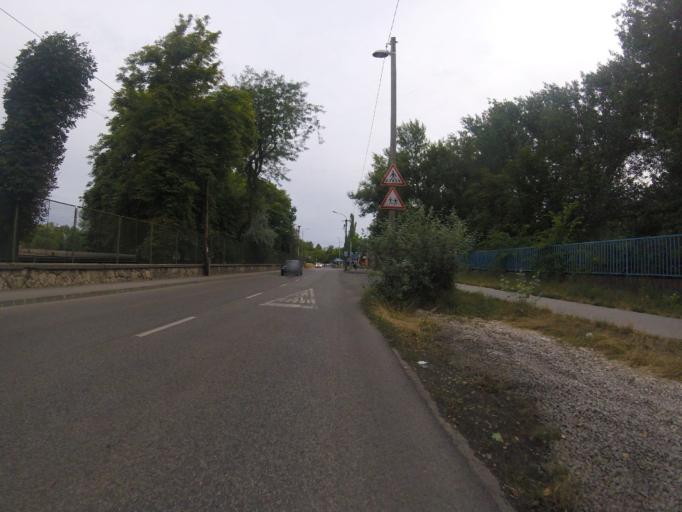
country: HU
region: Pest
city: Budakalasz
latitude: 47.5951
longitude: 19.0670
